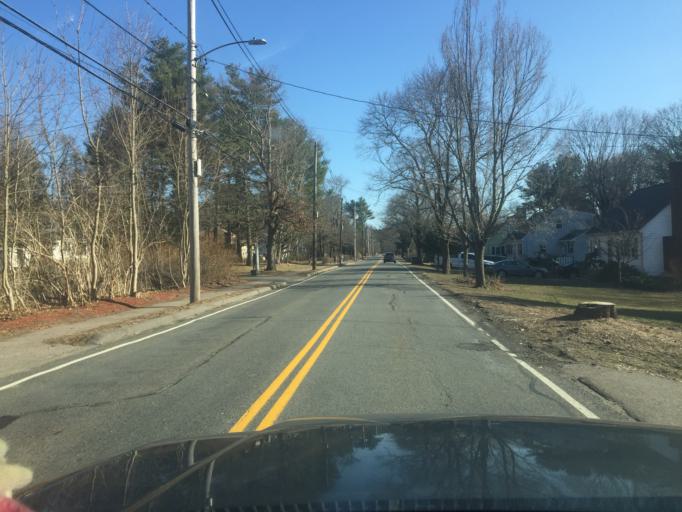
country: US
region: Massachusetts
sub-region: Norfolk County
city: Millis-Clicquot
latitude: 42.1615
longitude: -71.3541
